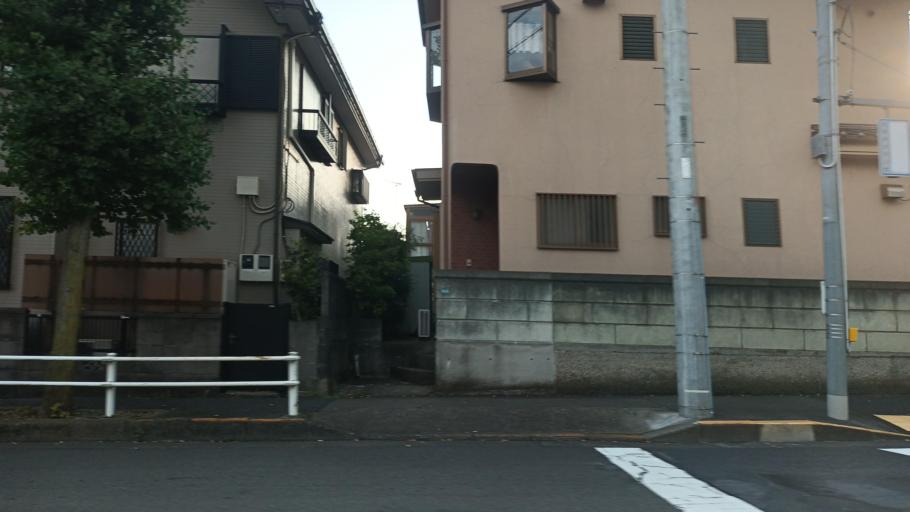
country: JP
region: Tokyo
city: Fussa
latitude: 35.7635
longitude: 139.3144
